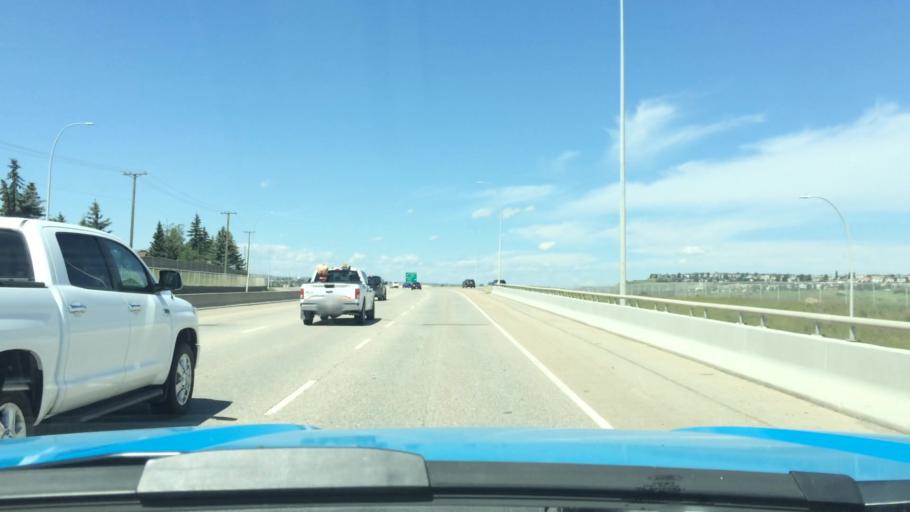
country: CA
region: Alberta
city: Calgary
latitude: 51.1361
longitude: -114.0755
